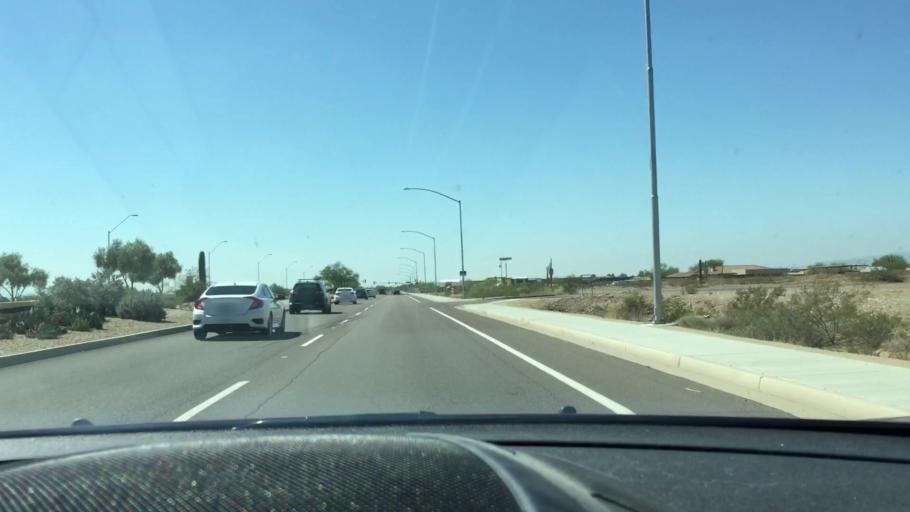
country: US
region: Arizona
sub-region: Maricopa County
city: Sun City West
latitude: 33.7005
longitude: -112.2731
